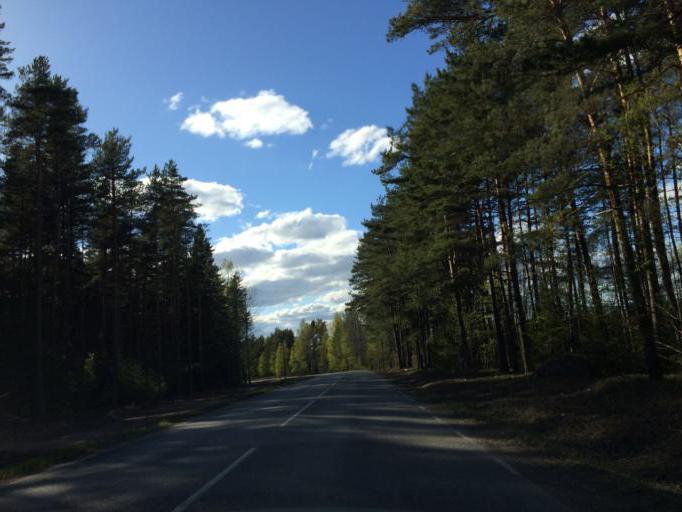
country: SE
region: Soedermanland
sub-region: Eskilstuna Kommun
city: Hallbybrunn
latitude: 59.4049
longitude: 16.3867
